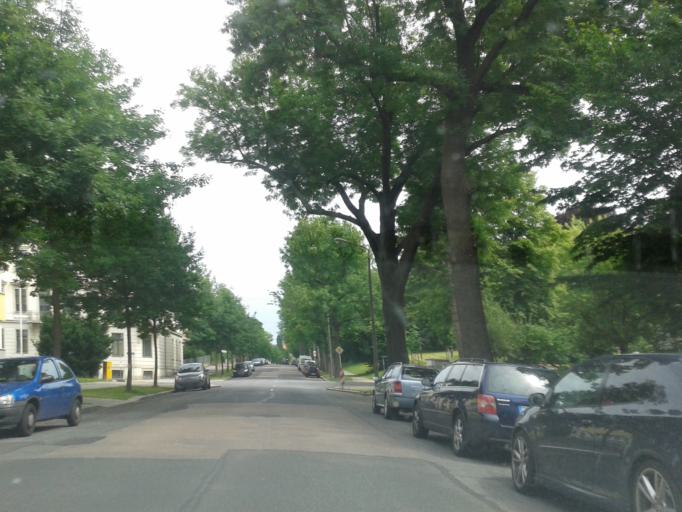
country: DE
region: Saxony
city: Dresden
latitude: 51.0324
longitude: 13.7411
